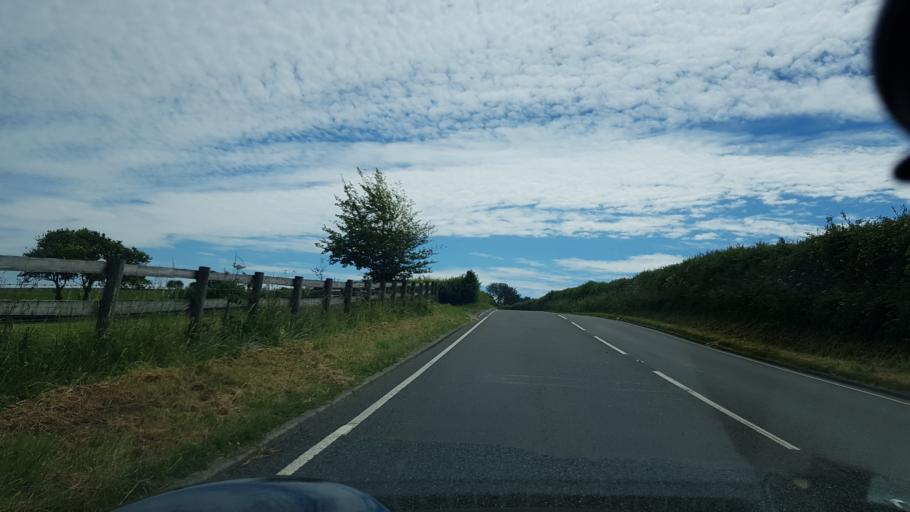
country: GB
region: Wales
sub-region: Carmarthenshire
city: Saint Clears
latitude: 51.7884
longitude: -4.4814
